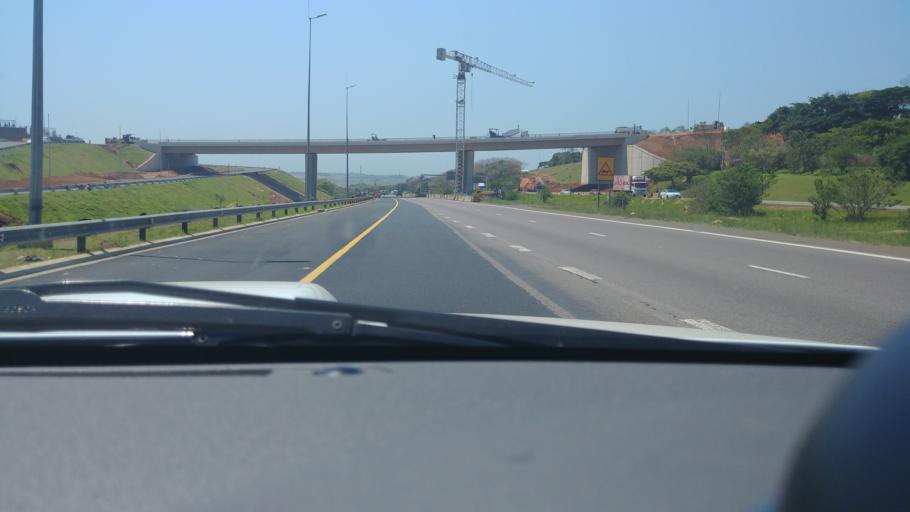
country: ZA
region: KwaZulu-Natal
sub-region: eThekwini Metropolitan Municipality
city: Durban
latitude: -29.7169
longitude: 31.0620
